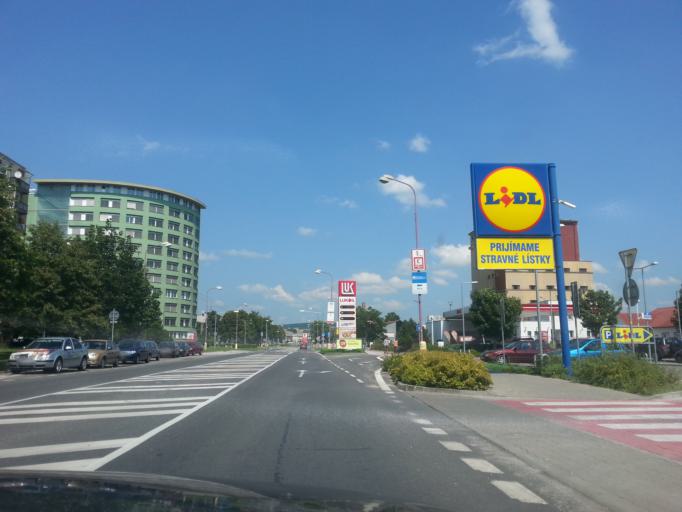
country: SK
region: Trenciansky
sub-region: Okres Nove Mesto nad Vahom
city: Nove Mesto nad Vahom
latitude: 48.7534
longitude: 17.8352
